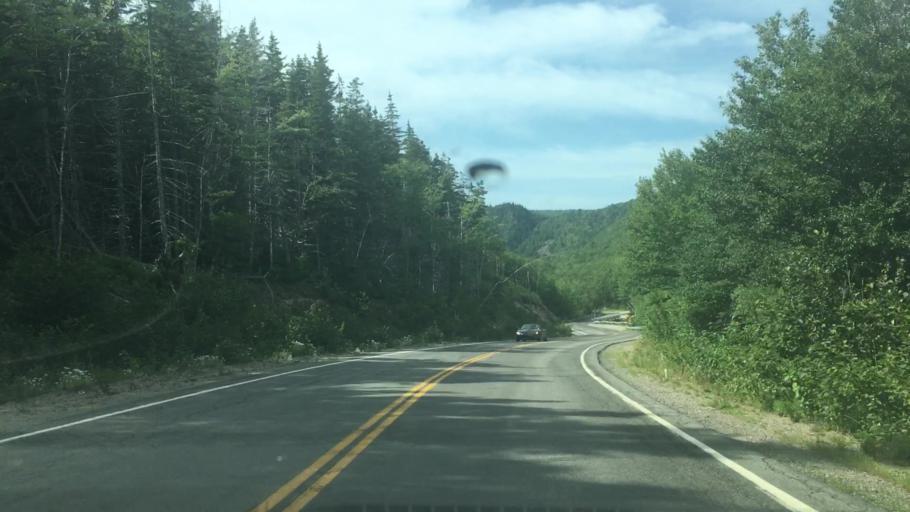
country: CA
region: Nova Scotia
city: Sydney Mines
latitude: 46.5822
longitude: -60.3935
